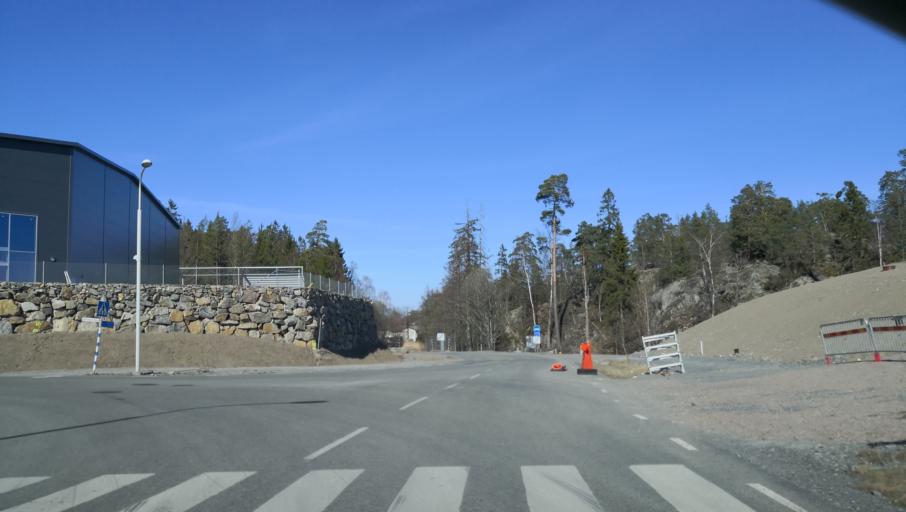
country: SE
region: Stockholm
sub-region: Varmdo Kommun
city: Gustavsberg
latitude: 59.3132
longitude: 18.3700
